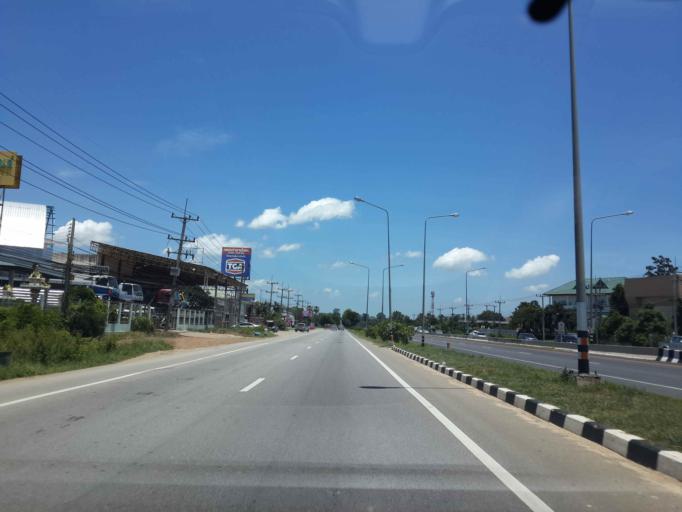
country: TH
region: Phetchaburi
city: Tha Yang
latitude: 12.9974
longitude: 99.9076
